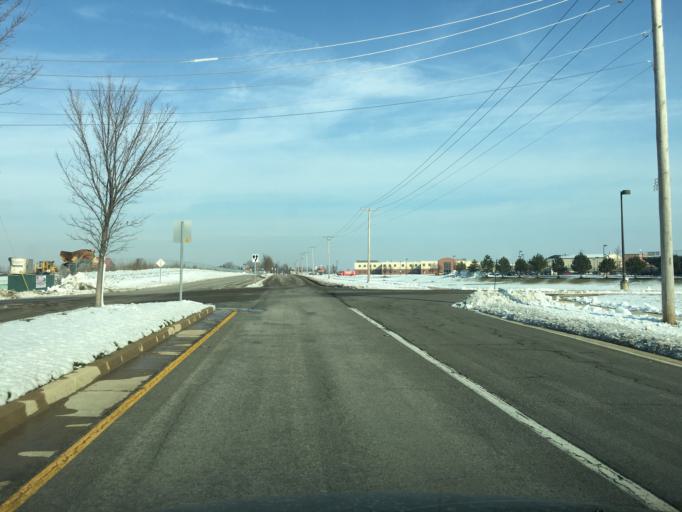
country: US
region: Illinois
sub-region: Will County
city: Plainfield
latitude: 41.6616
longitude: -88.1774
